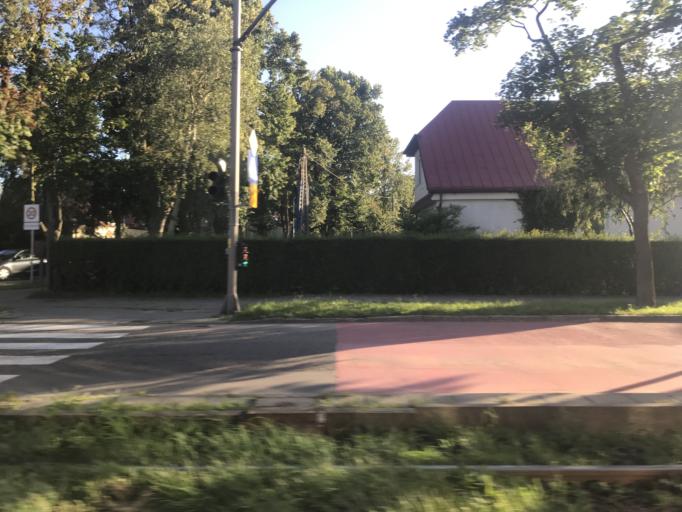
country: PL
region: Pomeranian Voivodeship
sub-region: Sopot
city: Sopot
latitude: 54.3923
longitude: 18.5762
